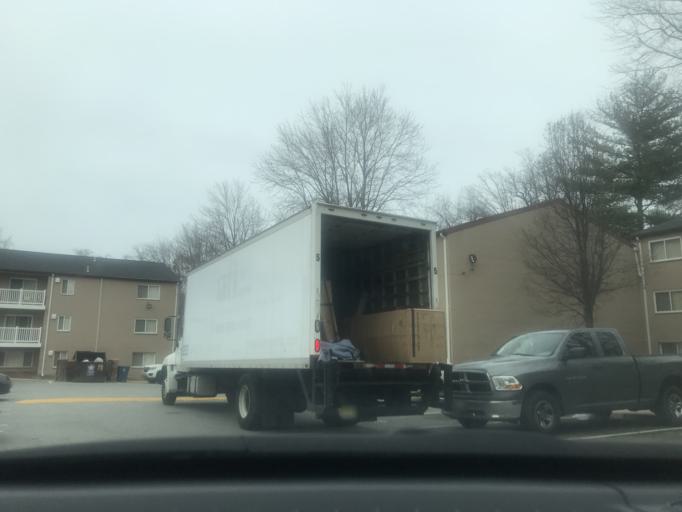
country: US
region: Maryland
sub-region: Prince George's County
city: Hillcrest Heights
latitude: 38.8137
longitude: -76.9687
